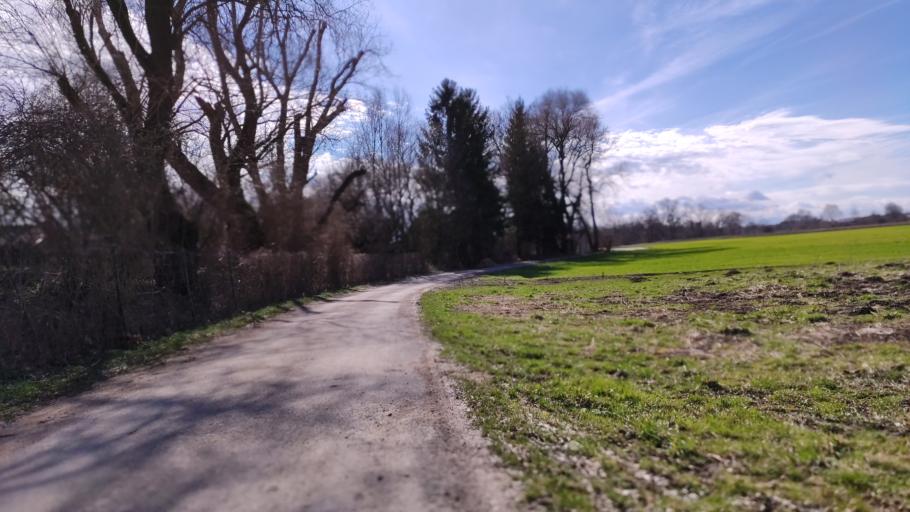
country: DE
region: Bavaria
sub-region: Upper Bavaria
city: Emmering
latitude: 48.1888
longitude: 11.2958
